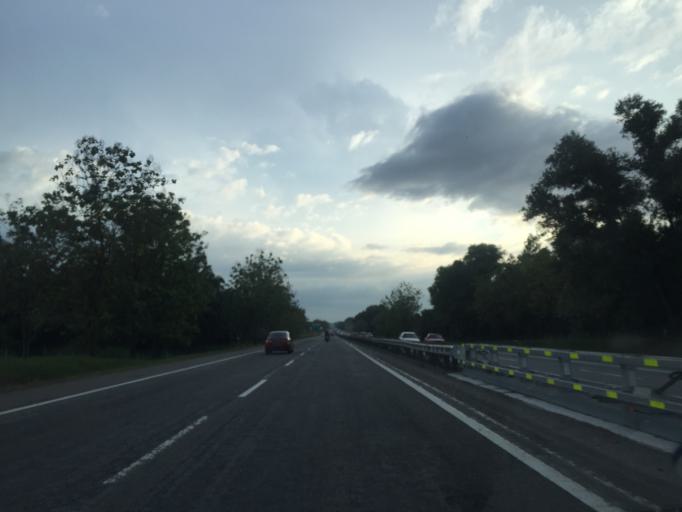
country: MY
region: Kedah
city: Bedong
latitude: 5.6980
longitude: 100.5228
